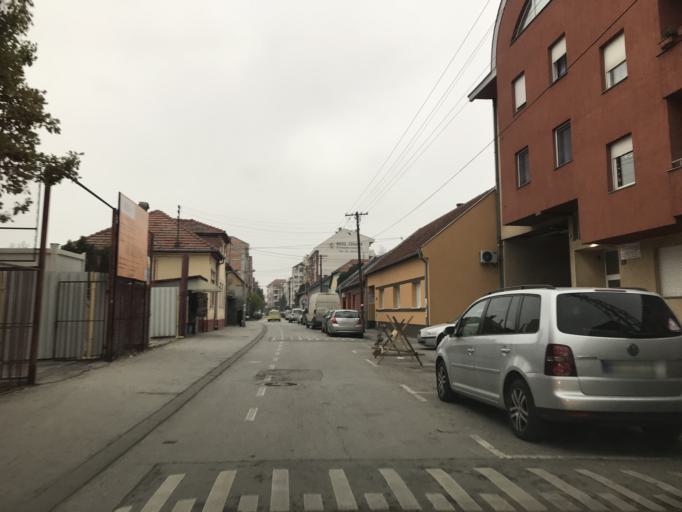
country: RS
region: Autonomna Pokrajina Vojvodina
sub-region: Juznobacki Okrug
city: Novi Sad
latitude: 45.2647
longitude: 19.8461
